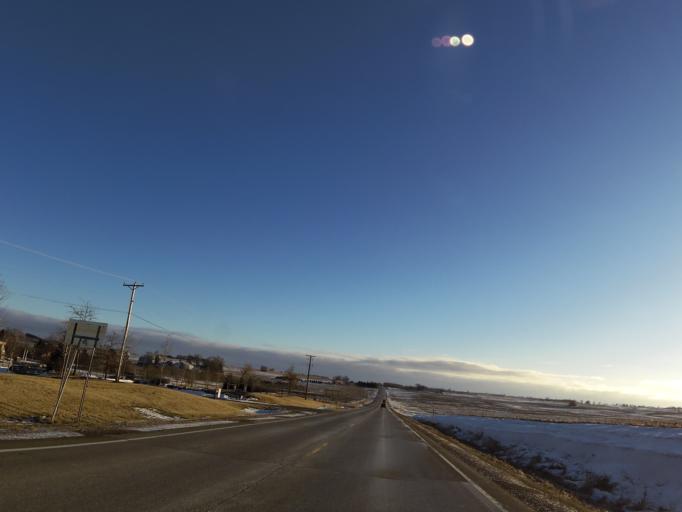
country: US
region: Minnesota
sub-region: Washington County
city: Cottage Grove
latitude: 44.8453
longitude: -92.8626
